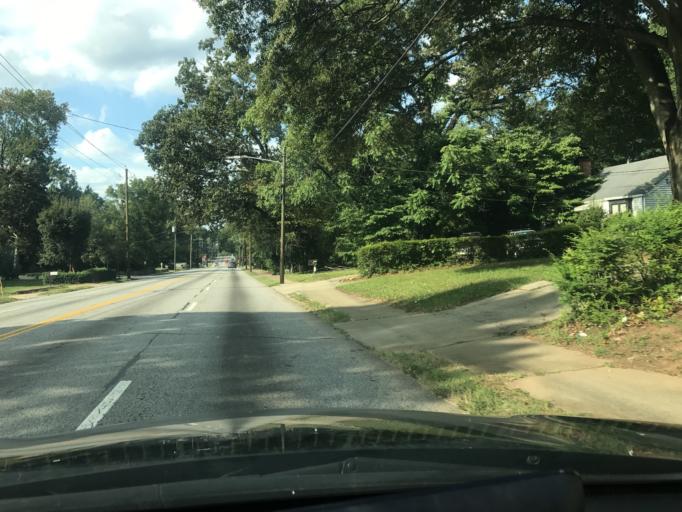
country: US
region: Georgia
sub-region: DeKalb County
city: Gresham Park
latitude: 33.7290
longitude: -84.3494
